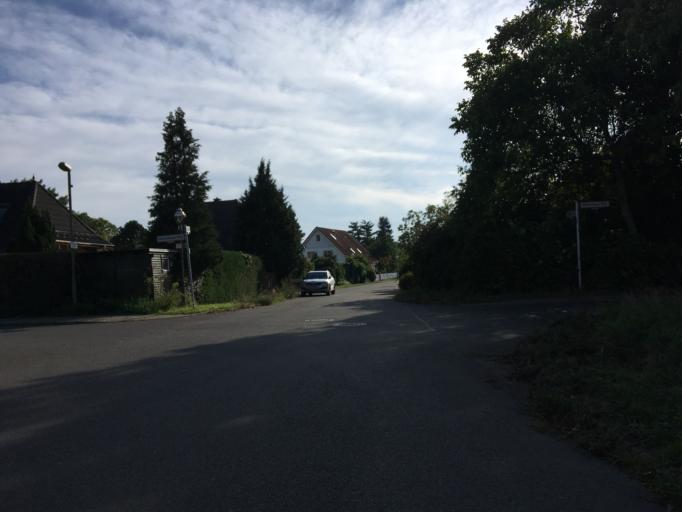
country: DE
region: Berlin
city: Kaulsdorf
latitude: 52.5110
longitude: 13.5825
